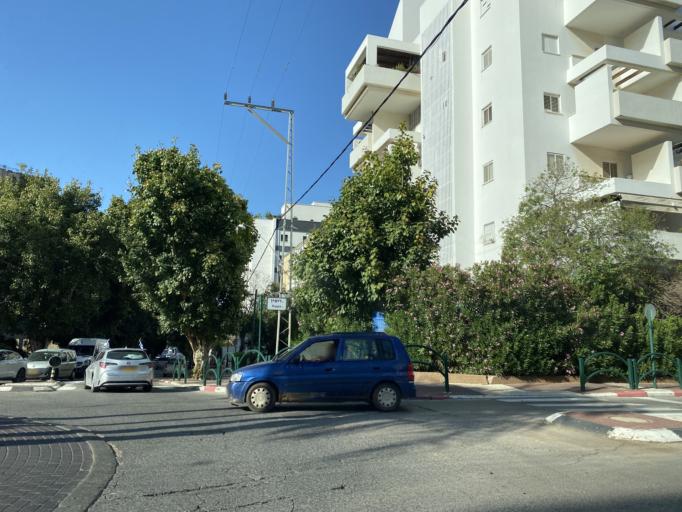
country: IL
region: Central District
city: Kfar Saba
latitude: 32.1711
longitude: 34.9132
